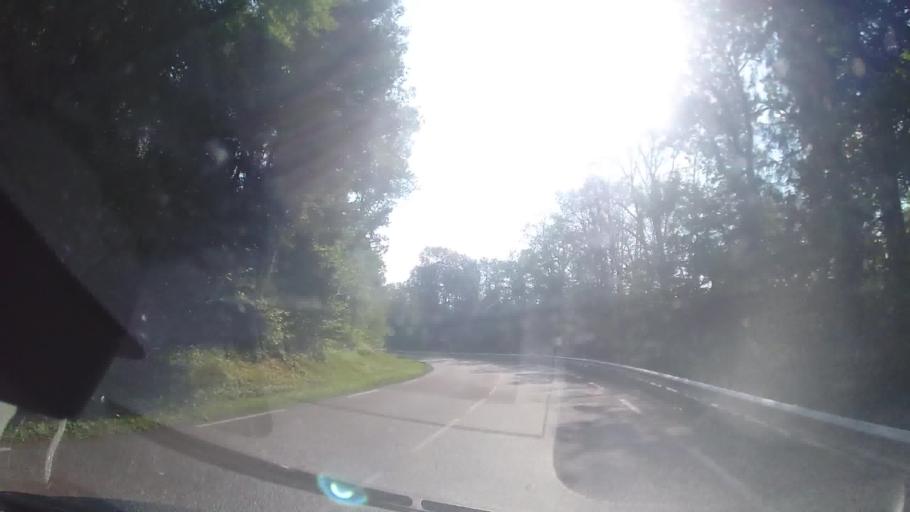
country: FR
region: Franche-Comte
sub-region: Departement du Jura
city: Clairvaux-les-Lacs
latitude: 46.5926
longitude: 5.8405
